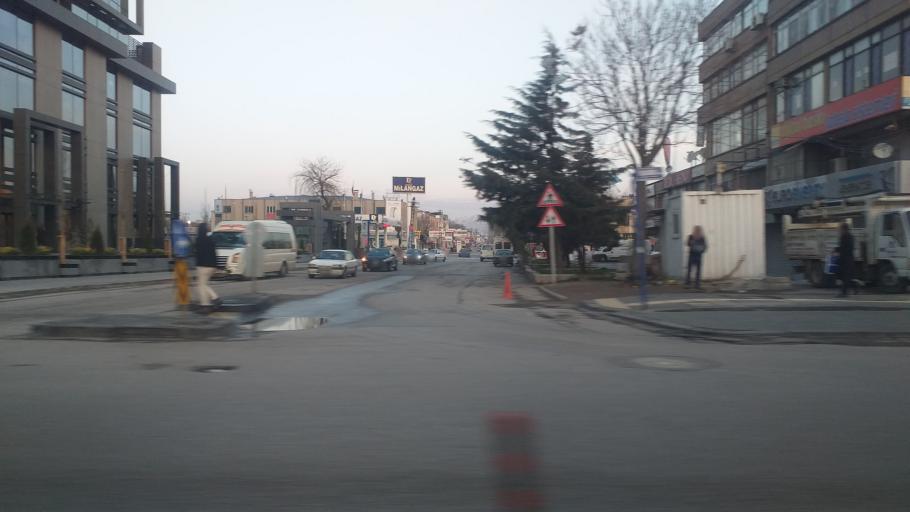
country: TR
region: Ankara
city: Ankara
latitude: 39.9449
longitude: 32.8470
